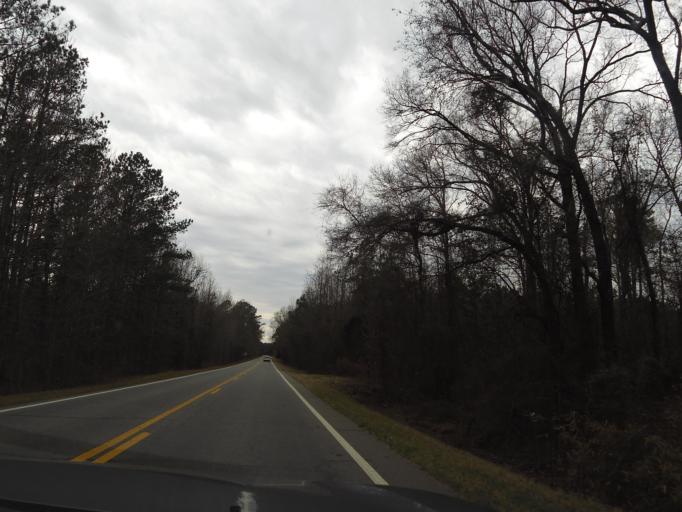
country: US
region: North Carolina
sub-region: Edgecombe County
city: Tarboro
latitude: 36.0084
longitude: -77.5260
